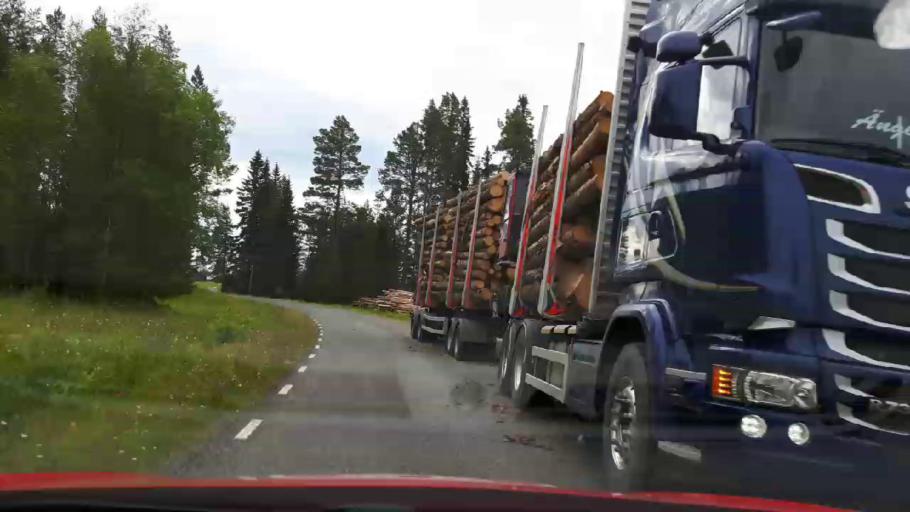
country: SE
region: Jaemtland
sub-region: OEstersunds Kommun
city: Lit
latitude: 63.3908
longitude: 15.0142
